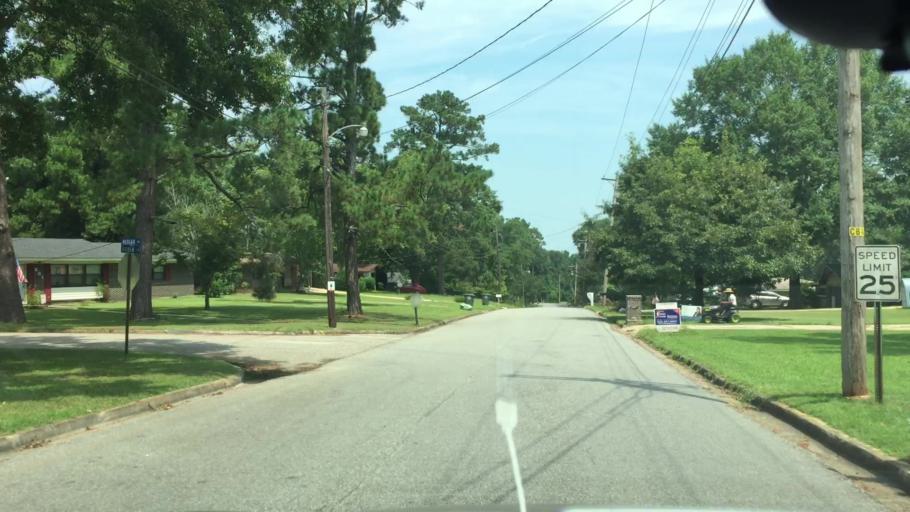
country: US
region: Alabama
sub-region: Coffee County
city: Enterprise
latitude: 31.3319
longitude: -85.8122
